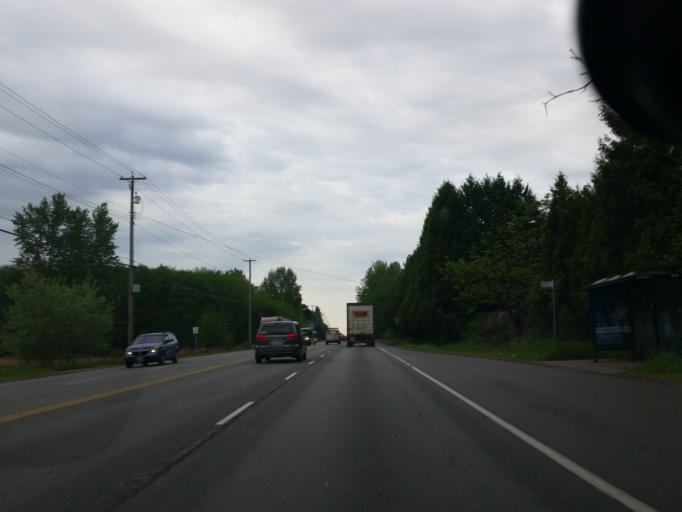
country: CA
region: British Columbia
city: Walnut Grove
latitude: 49.1408
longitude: -122.6684
